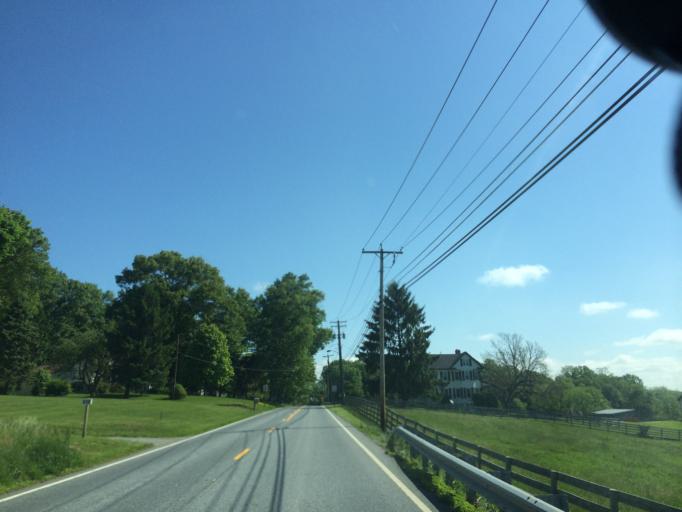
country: US
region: Maryland
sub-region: Carroll County
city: Hampstead
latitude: 39.5362
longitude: -76.8502
